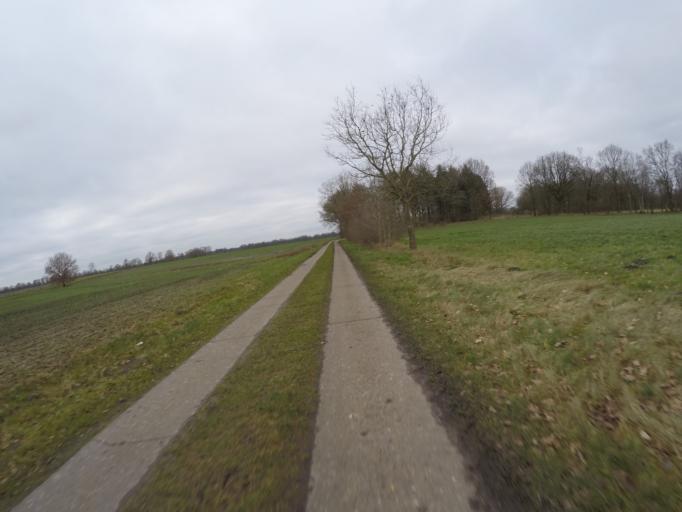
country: DE
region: Schleswig-Holstein
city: Hemdingen
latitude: 53.7756
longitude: 9.8410
